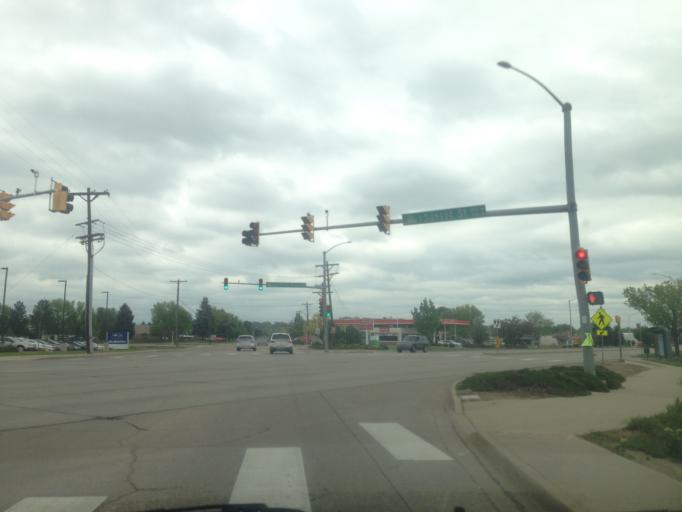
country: US
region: Colorado
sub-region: Boulder County
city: Longmont
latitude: 40.1483
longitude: -105.1214
